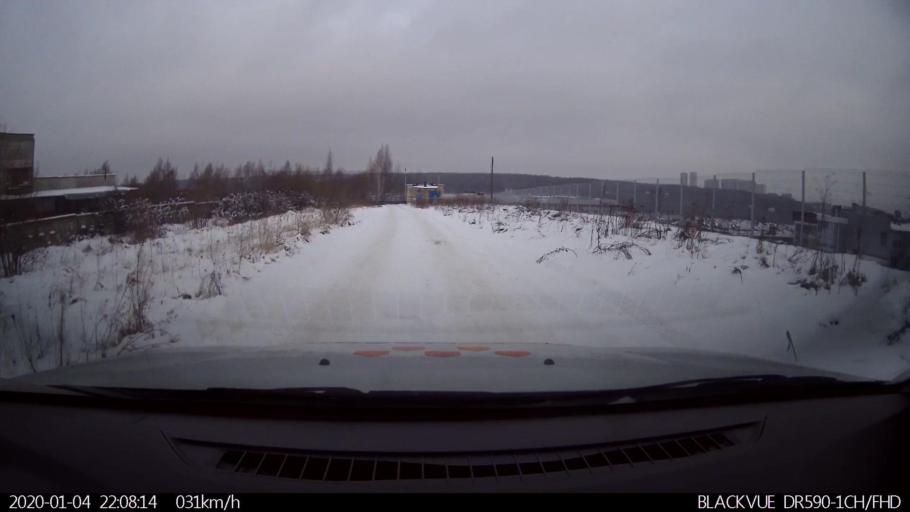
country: RU
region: Nizjnij Novgorod
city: Afonino
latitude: 56.2352
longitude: 44.0161
